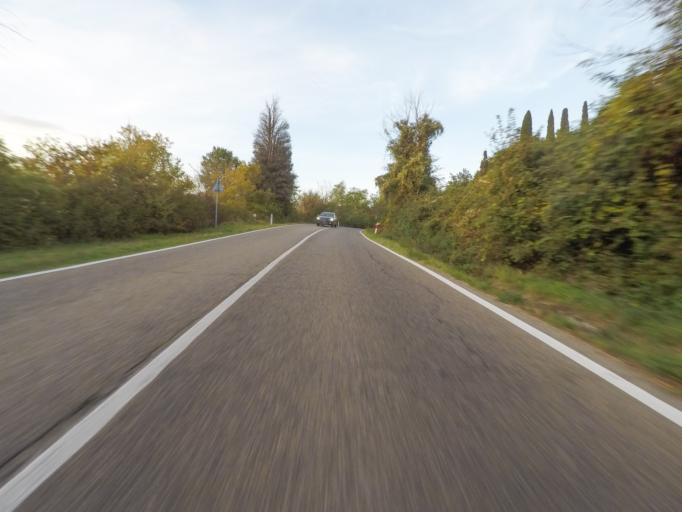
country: IT
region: Tuscany
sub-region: Provincia di Siena
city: Pienza
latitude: 43.1007
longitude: 11.6966
